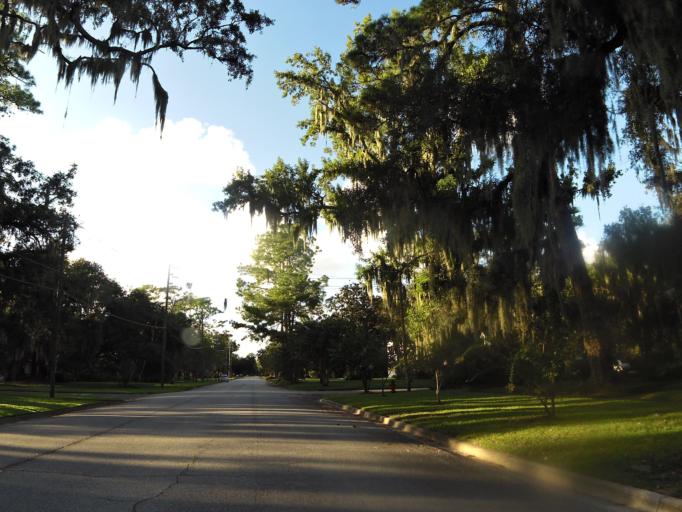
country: US
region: Georgia
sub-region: Glynn County
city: Brunswick
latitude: 31.1342
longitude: -81.4878
